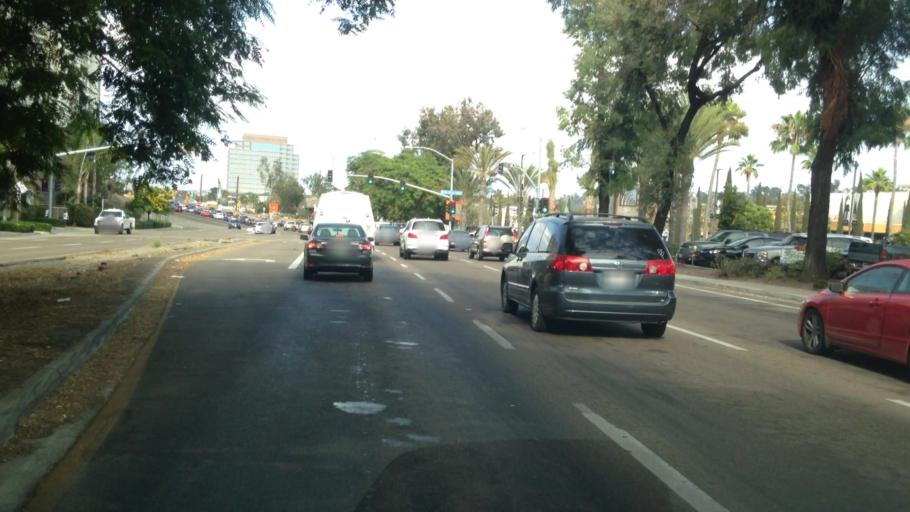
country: US
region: California
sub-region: San Diego County
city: San Diego
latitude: 32.7698
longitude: -117.1664
